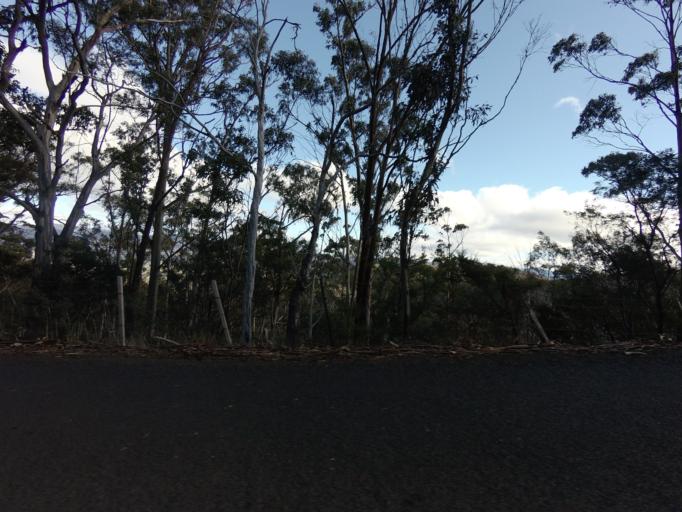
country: AU
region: Tasmania
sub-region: Derwent Valley
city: New Norfolk
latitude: -42.7274
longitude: 147.0300
